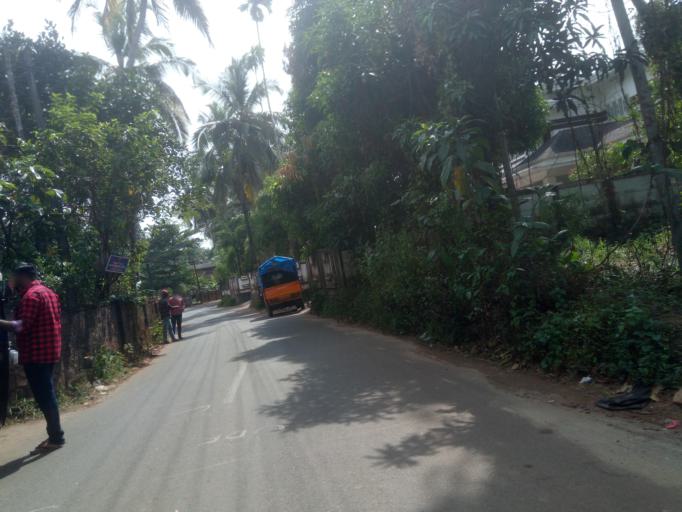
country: IN
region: Kerala
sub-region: Malappuram
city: Ponnani
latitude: 10.8091
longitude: 76.0323
